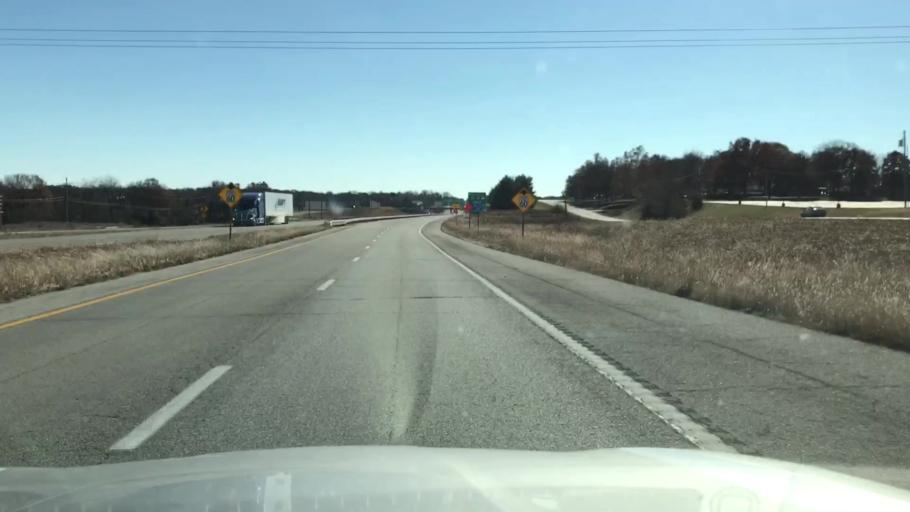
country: US
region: Missouri
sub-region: Jasper County
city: Carthage
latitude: 37.0897
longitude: -94.3124
